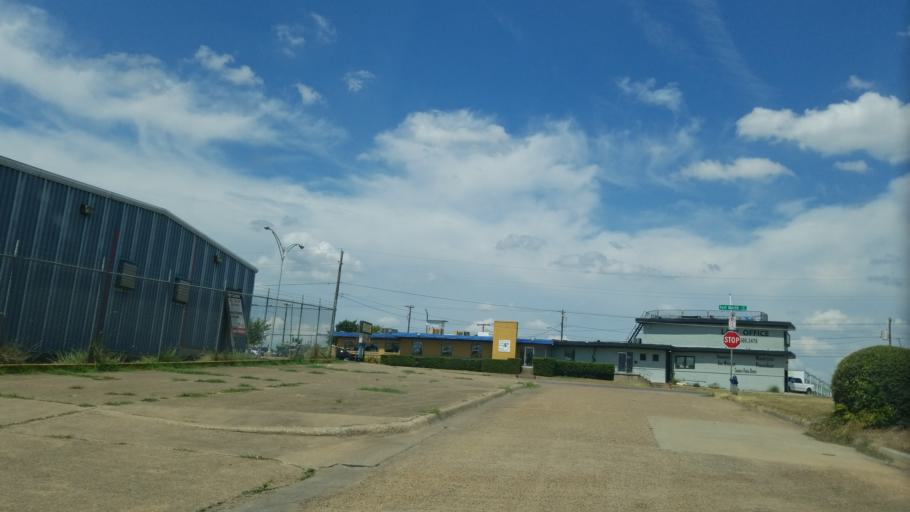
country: US
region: Texas
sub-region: Dallas County
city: Cockrell Hill
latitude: 32.7633
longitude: -96.8527
